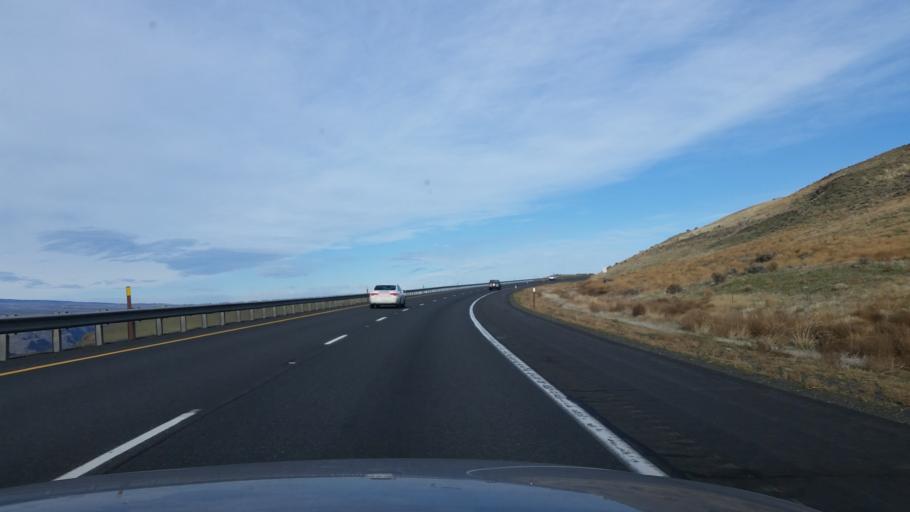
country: US
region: Washington
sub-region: Grant County
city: Quincy
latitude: 46.9981
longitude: -119.9738
